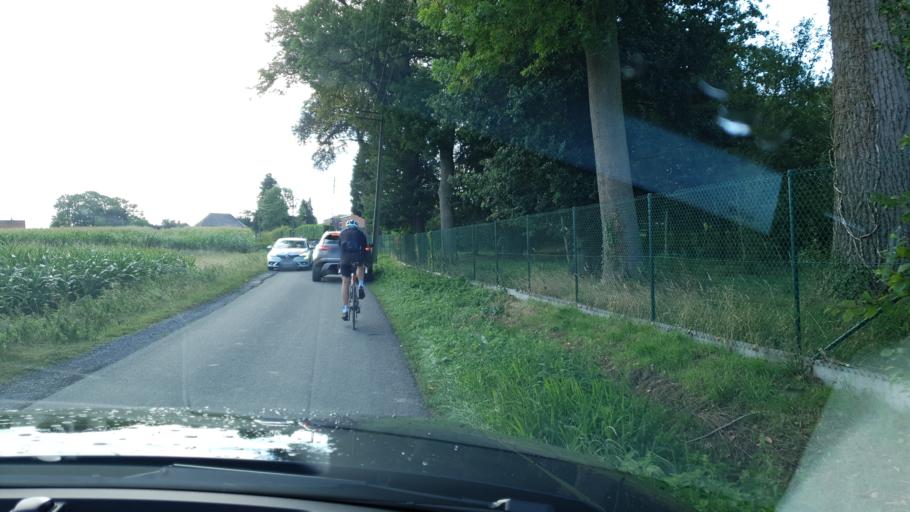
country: BE
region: Wallonia
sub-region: Province du Hainaut
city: Tournai
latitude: 50.6636
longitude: 3.3970
